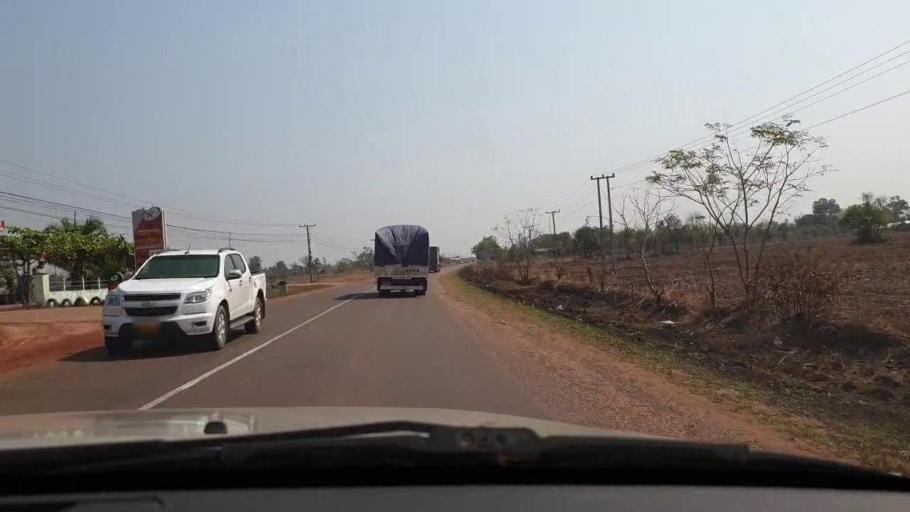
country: TH
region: Nong Khai
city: Phon Phisai
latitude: 18.0765
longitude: 102.9134
